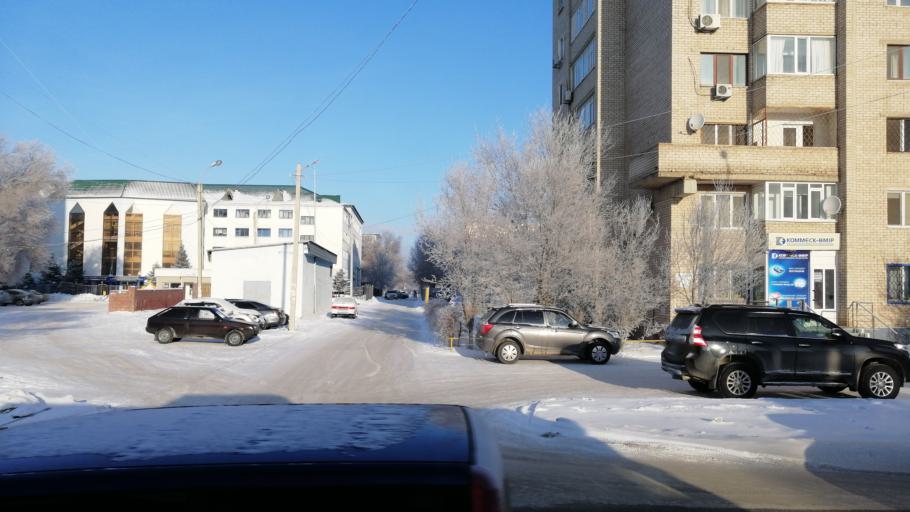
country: KZ
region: Aqtoebe
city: Aqtobe
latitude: 50.3005
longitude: 57.1510
